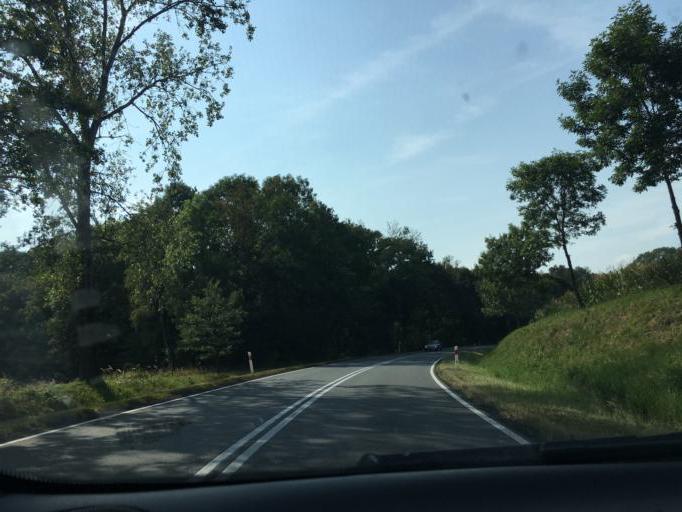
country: PL
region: Opole Voivodeship
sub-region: Powiat nyski
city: Nysa
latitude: 50.4331
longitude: 17.4129
